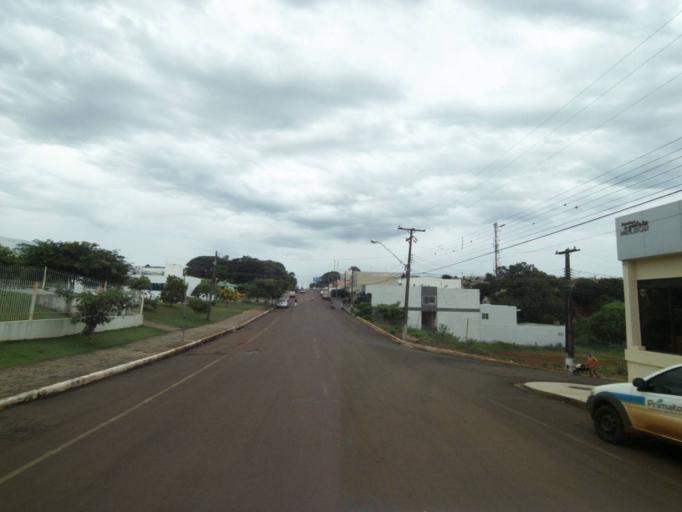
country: BR
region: Parana
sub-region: Guaraniacu
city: Guaraniacu
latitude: -25.1003
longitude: -52.8707
